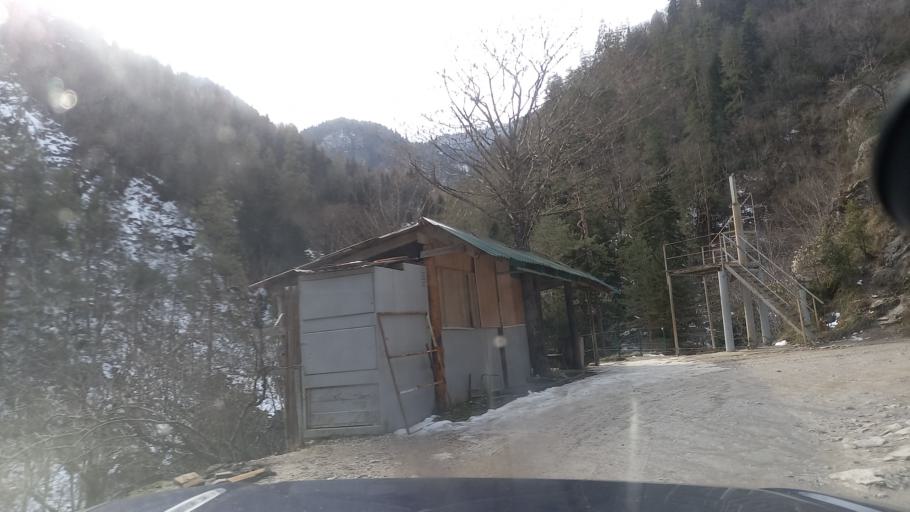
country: GE
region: Abkhazia
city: Gagra
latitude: 43.4103
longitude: 40.4599
